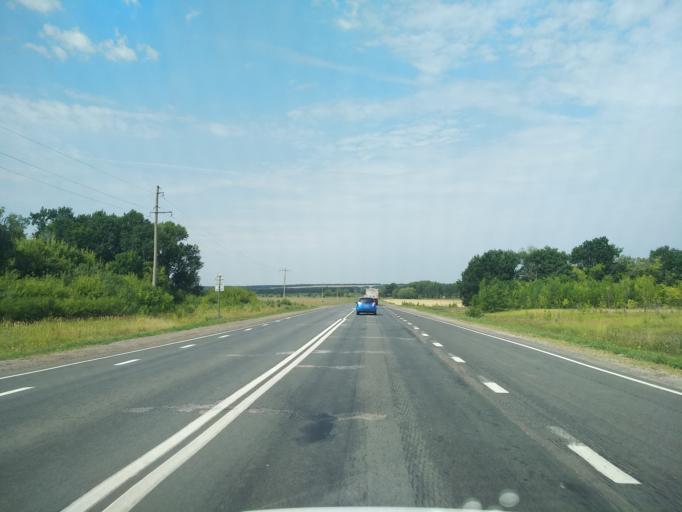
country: RU
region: Voronezj
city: Orlovo
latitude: 51.6798
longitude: 39.6236
